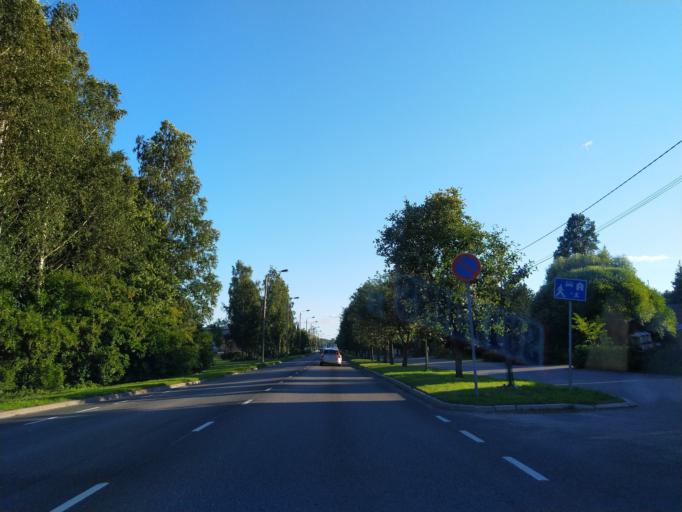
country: FI
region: Varsinais-Suomi
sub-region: Turku
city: Kaarina
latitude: 60.4440
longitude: 22.3254
